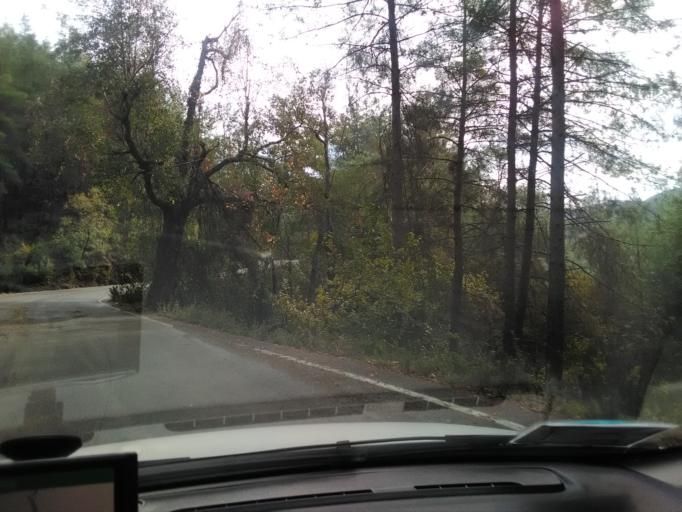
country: TR
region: Antalya
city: Gazipasa
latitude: 36.2430
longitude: 32.4159
